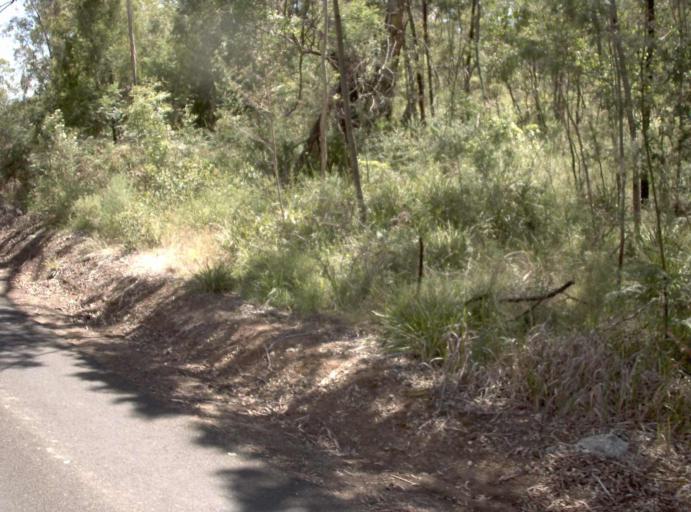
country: AU
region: Victoria
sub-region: East Gippsland
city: Lakes Entrance
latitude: -37.4391
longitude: 148.1910
